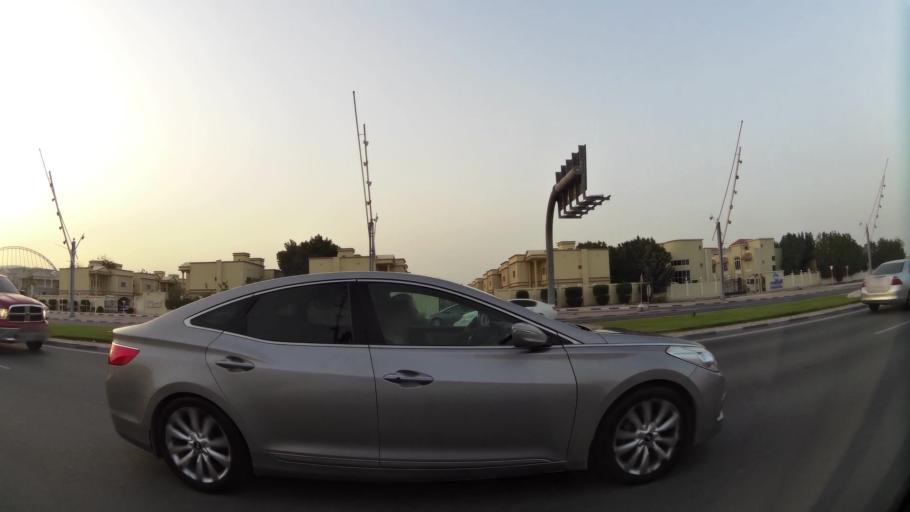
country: QA
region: Baladiyat ar Rayyan
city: Ar Rayyan
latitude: 25.2621
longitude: 51.4575
